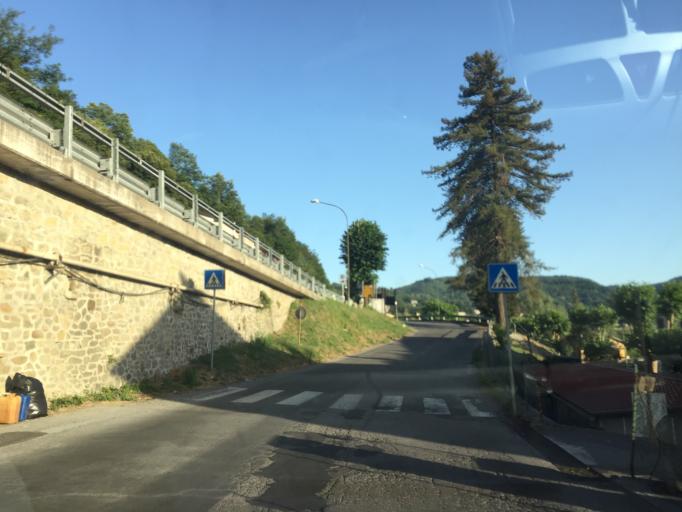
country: IT
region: Tuscany
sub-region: Provincia di Lucca
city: Castelnuovo di Garfagnana
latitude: 44.1173
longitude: 10.4096
